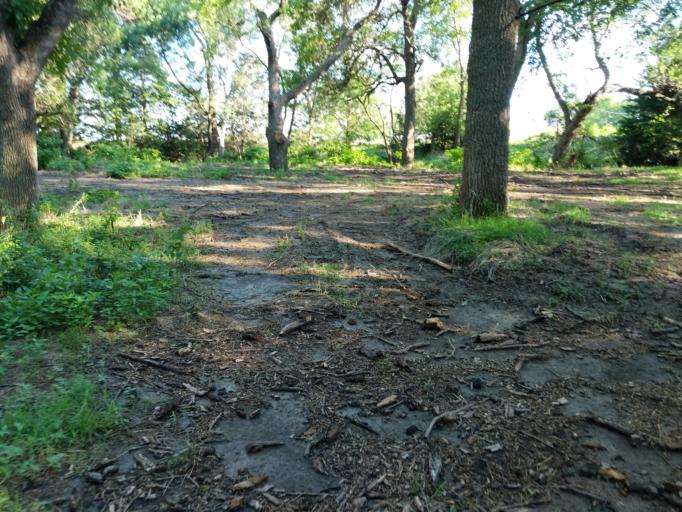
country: US
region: Kansas
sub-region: Smith County
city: Smith Center
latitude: 39.8910
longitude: -98.9471
